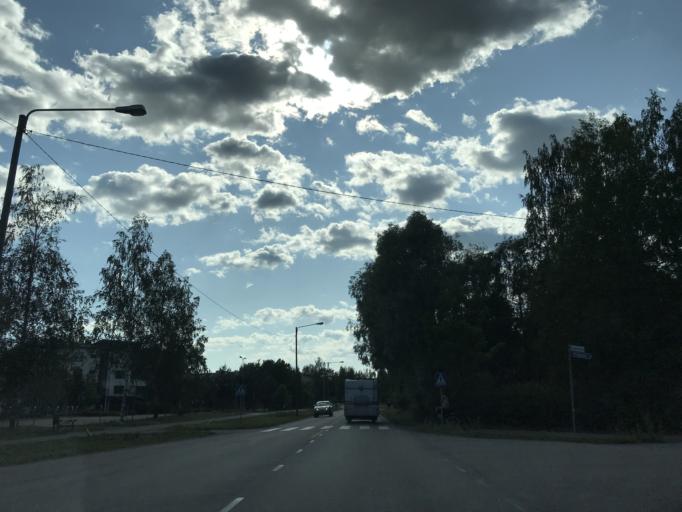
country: FI
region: Uusimaa
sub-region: Helsinki
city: Nurmijaervi
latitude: 60.4653
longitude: 24.8059
